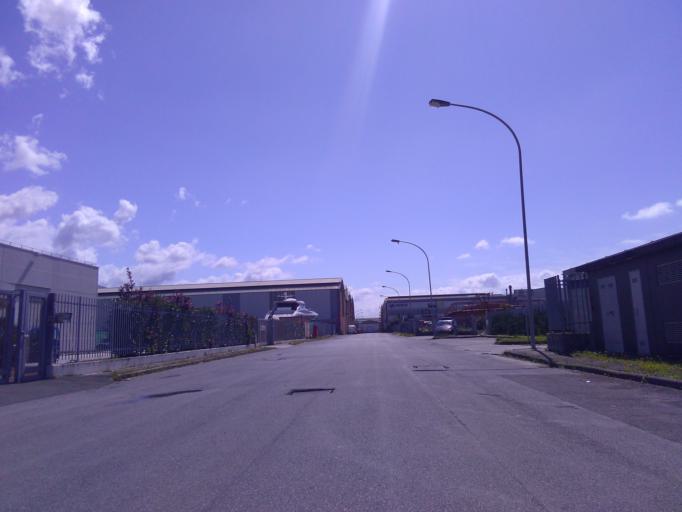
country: IT
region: Tuscany
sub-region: Provincia di Massa-Carrara
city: Massa
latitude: 44.0286
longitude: 10.0986
